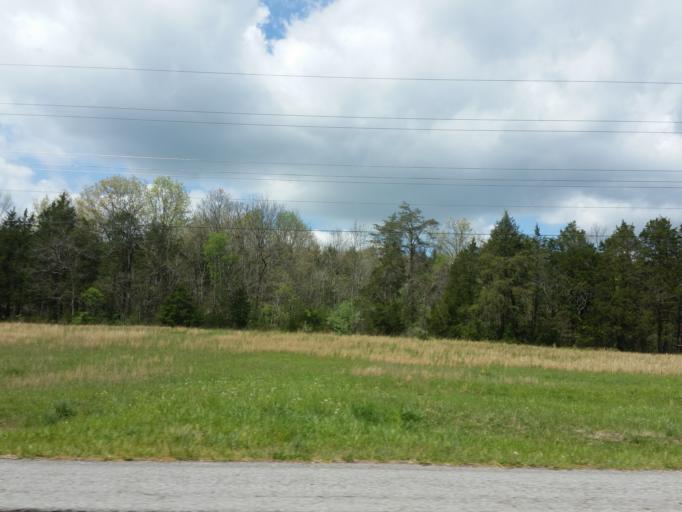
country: US
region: Tennessee
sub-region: Claiborne County
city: Harrogate
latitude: 36.5309
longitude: -83.7092
